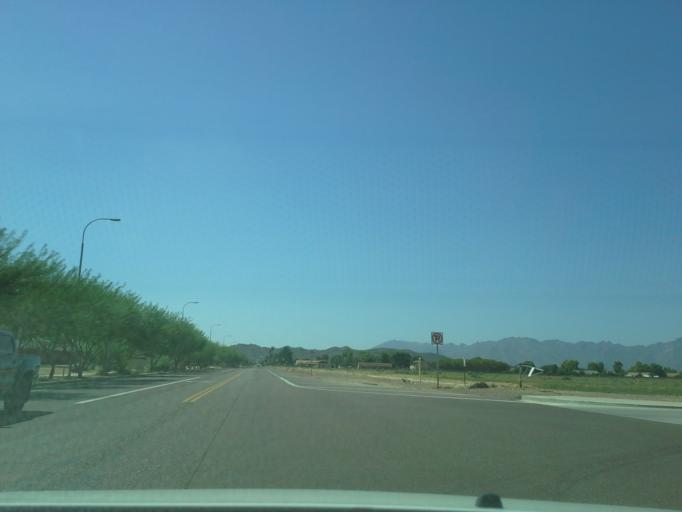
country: US
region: Arizona
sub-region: Maricopa County
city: Laveen
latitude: 33.3743
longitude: -112.1520
